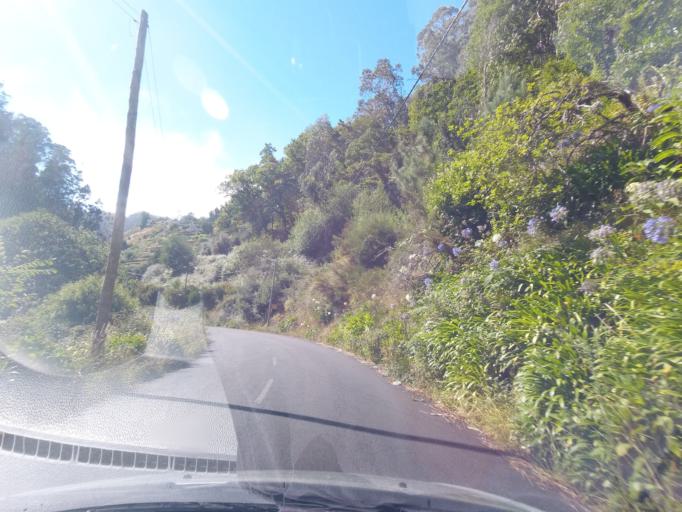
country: PT
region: Madeira
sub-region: Santa Cruz
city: Camacha
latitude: 32.6916
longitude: -16.8513
